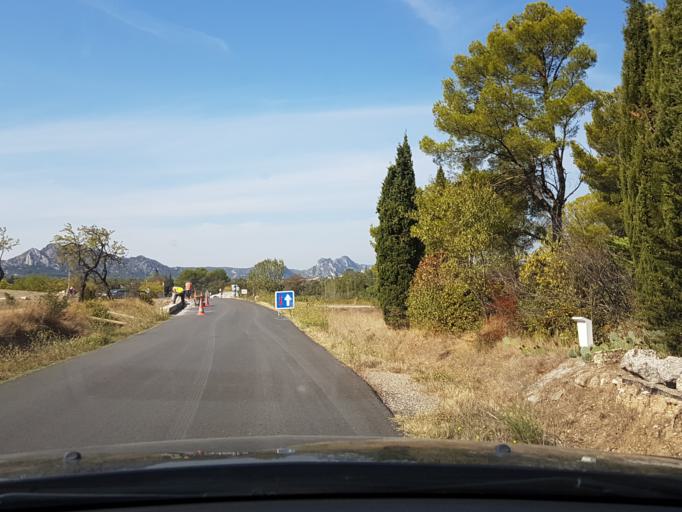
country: FR
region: Provence-Alpes-Cote d'Azur
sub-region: Departement des Bouches-du-Rhone
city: Eygalieres
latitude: 43.7635
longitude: 4.9679
